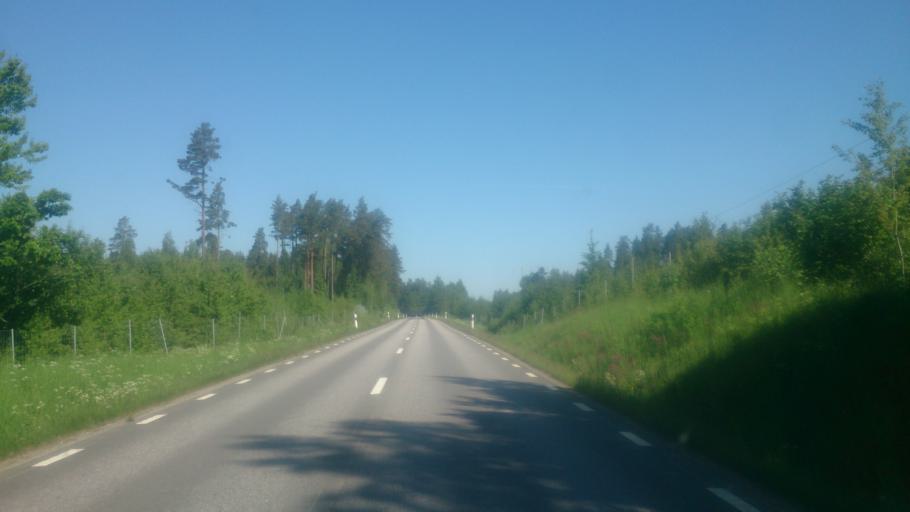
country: SE
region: OEstergoetland
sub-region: Atvidabergs Kommun
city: Atvidaberg
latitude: 58.1593
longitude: 16.0660
